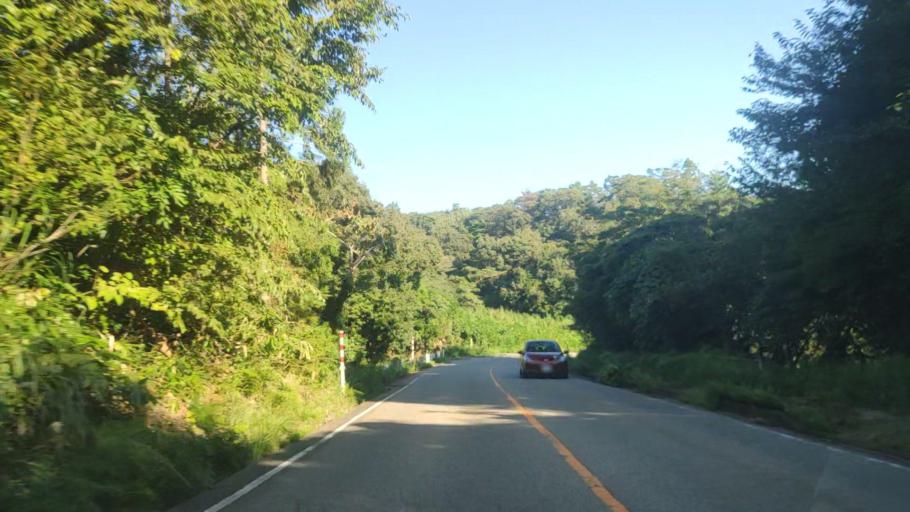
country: JP
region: Ishikawa
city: Nanao
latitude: 37.1006
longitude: 136.9492
